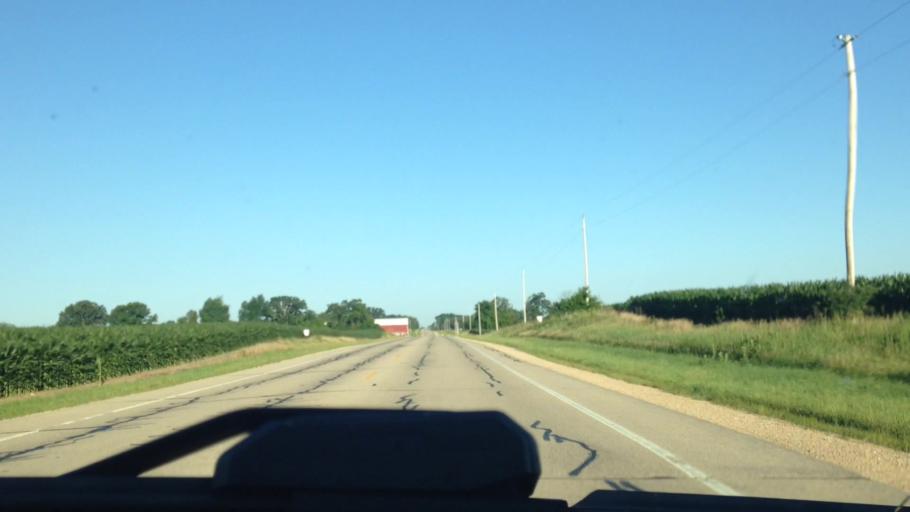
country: US
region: Wisconsin
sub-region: Columbia County
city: Columbus
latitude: 43.3417
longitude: -89.0544
